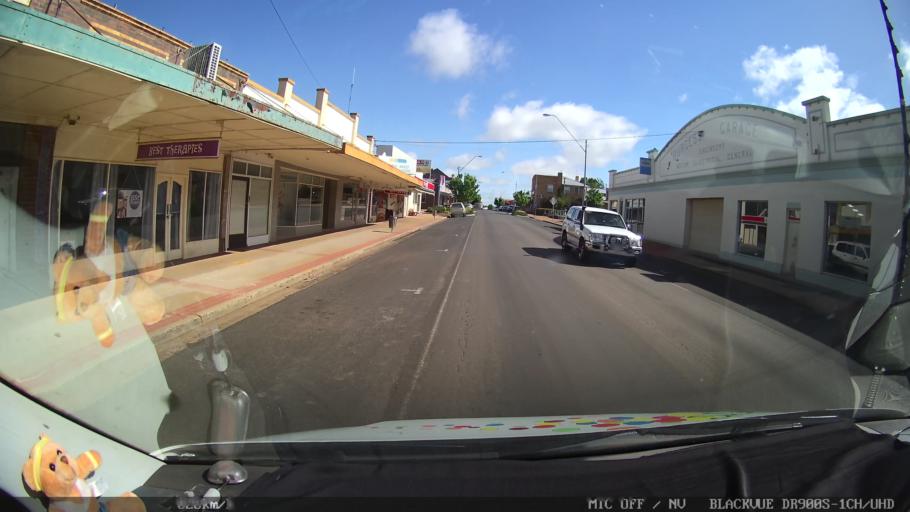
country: AU
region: New South Wales
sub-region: Guyra
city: Guyra
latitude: -30.2203
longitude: 151.6715
